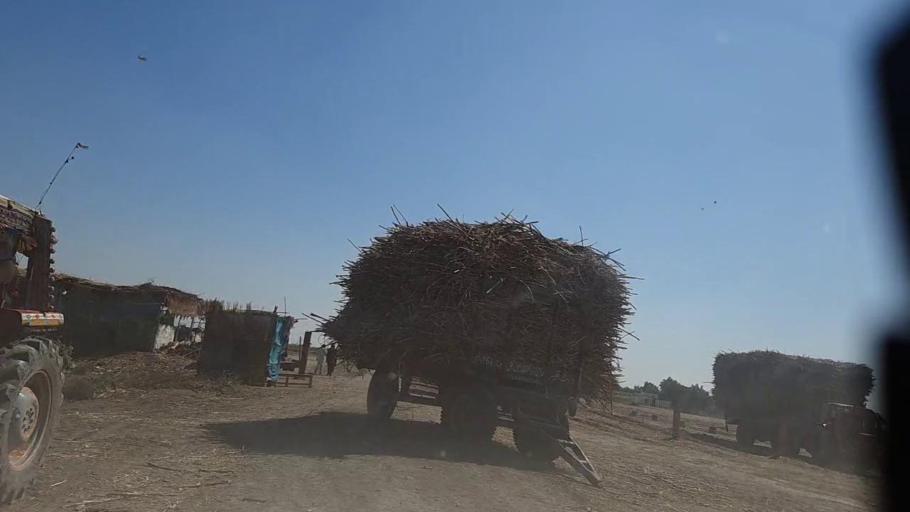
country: PK
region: Sindh
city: Digri
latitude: 25.1624
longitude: 69.0395
